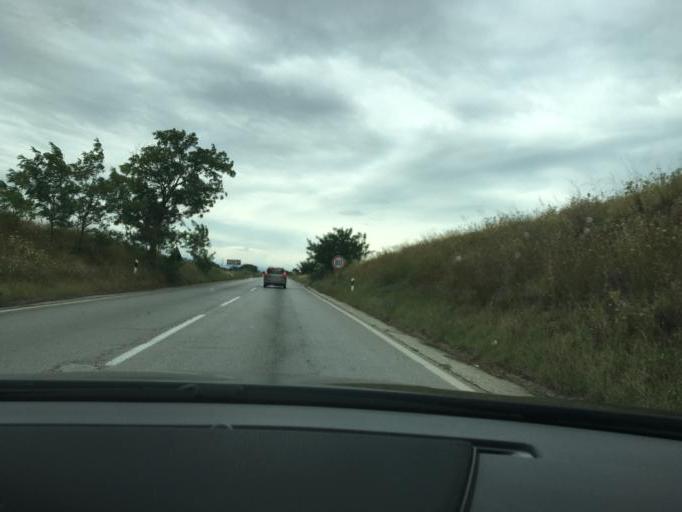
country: MK
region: Staro Nagoricane
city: Staro Nagorichane
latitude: 42.1731
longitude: 21.7986
